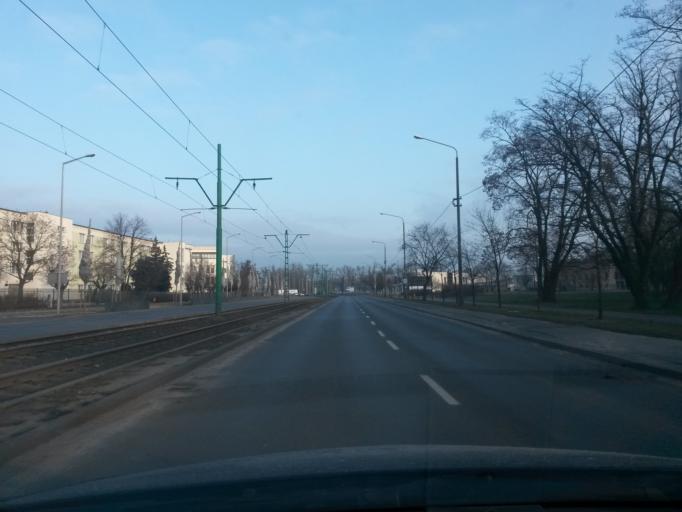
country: PL
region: Greater Poland Voivodeship
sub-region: Poznan
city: Poznan
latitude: 52.4002
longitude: 16.9532
